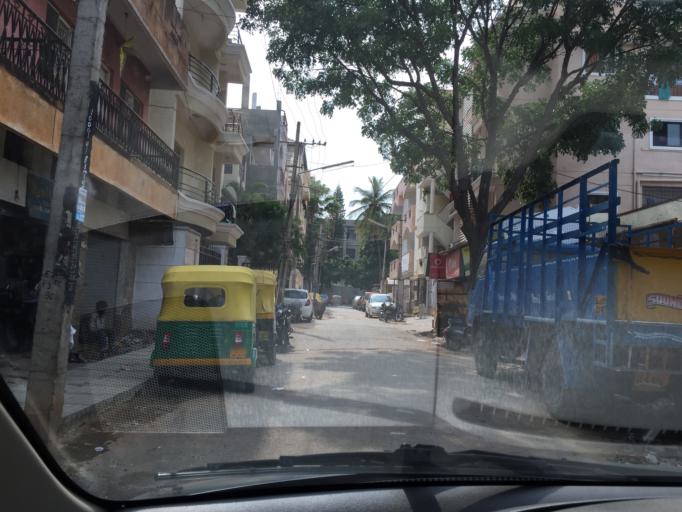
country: IN
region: Karnataka
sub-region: Bangalore Urban
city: Bangalore
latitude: 13.0060
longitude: 77.6237
